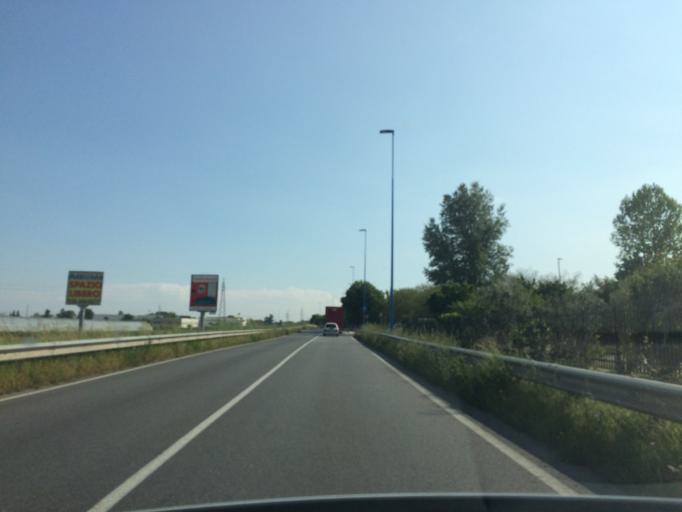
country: IT
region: Lombardy
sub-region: Provincia di Brescia
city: Folzano
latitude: 45.5090
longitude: 10.2153
